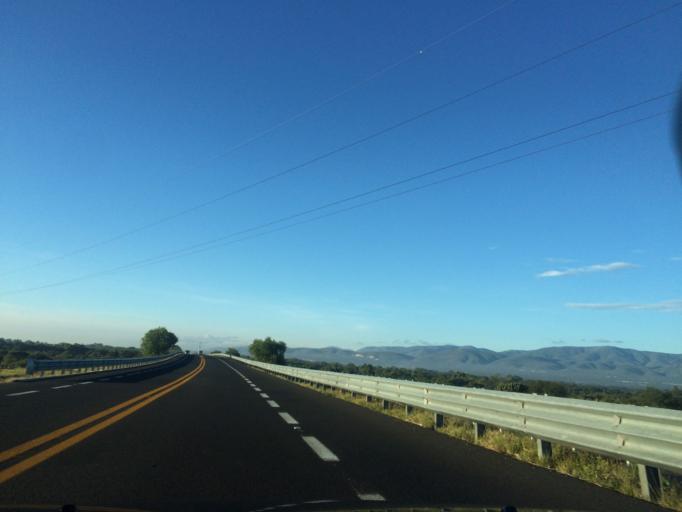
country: MX
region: Puebla
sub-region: Tehuacan
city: Magdalena Cuayucatepec
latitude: 18.5485
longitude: -97.4625
